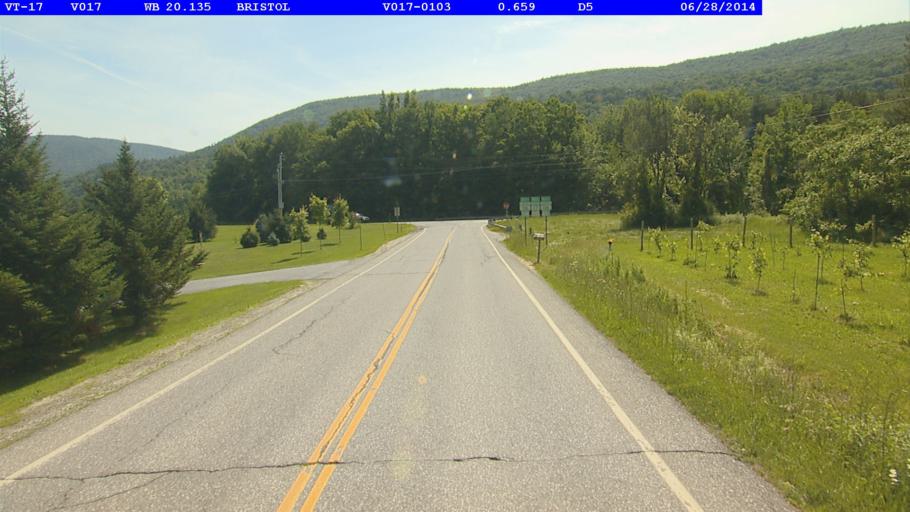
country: US
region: Vermont
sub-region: Addison County
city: Bristol
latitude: 44.1536
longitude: -73.0446
